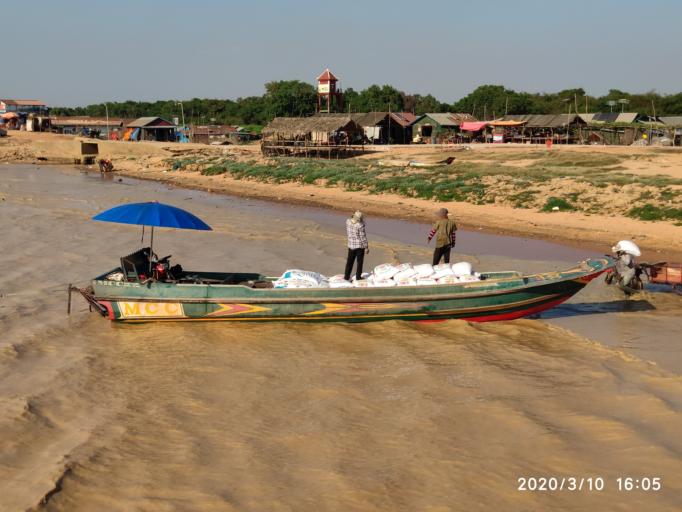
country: KH
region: Siem Reap
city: Siem Reap
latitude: 13.2534
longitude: 103.8228
